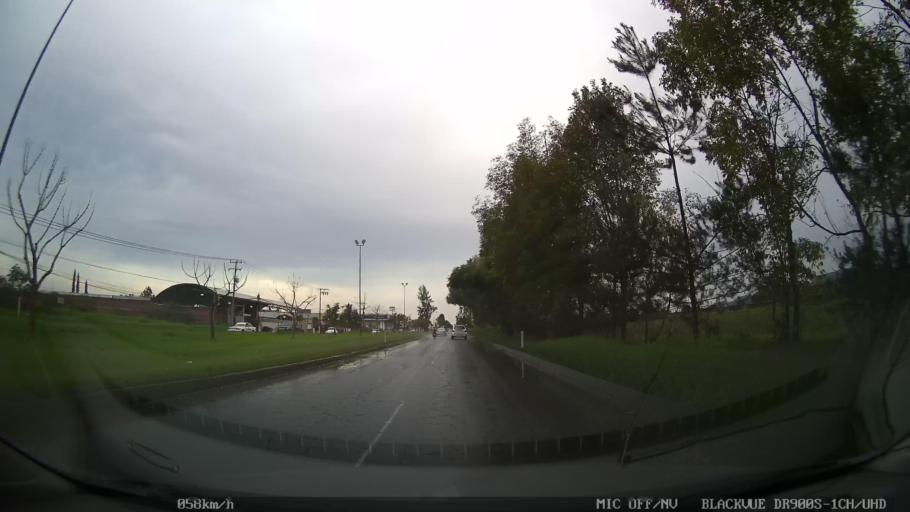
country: MX
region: Michoacan
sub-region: Uruapan
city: Santa Rosa (Santa Barbara)
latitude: 19.3923
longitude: -102.0386
